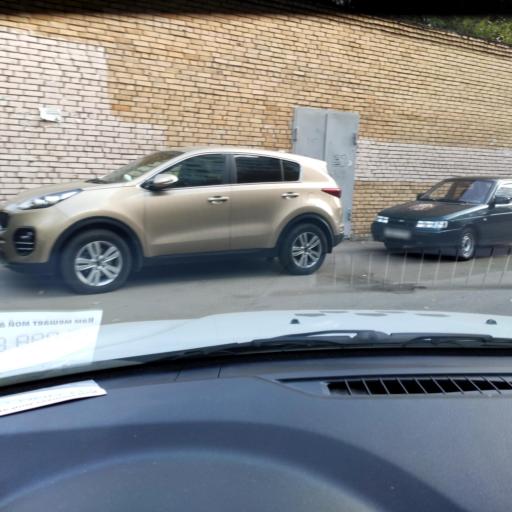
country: RU
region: Samara
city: Tol'yatti
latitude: 53.5297
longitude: 49.3335
